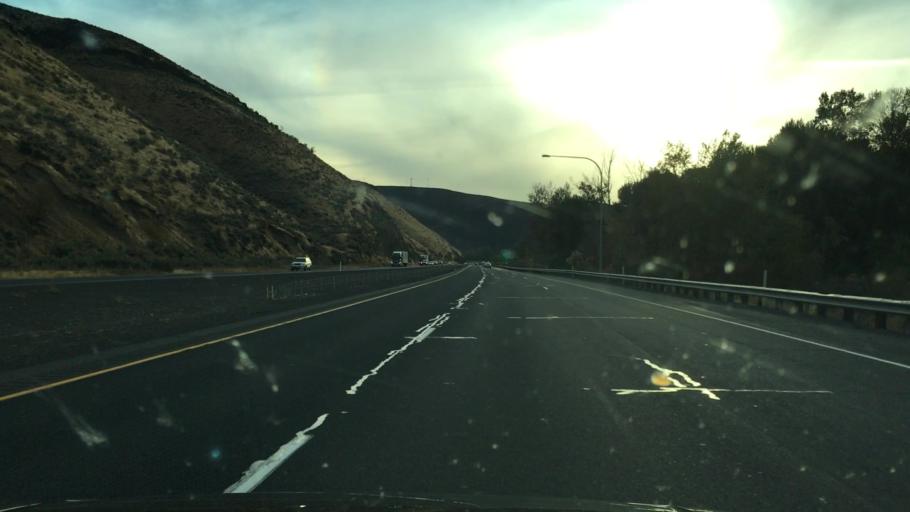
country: US
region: Washington
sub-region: Yakima County
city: Selah
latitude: 46.6452
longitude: -120.5088
